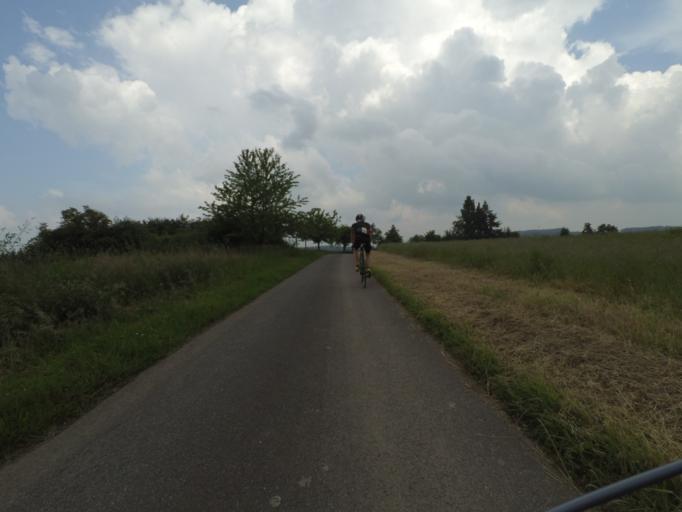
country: DE
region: Rheinland-Pfalz
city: Buch
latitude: 50.0548
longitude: 7.3811
